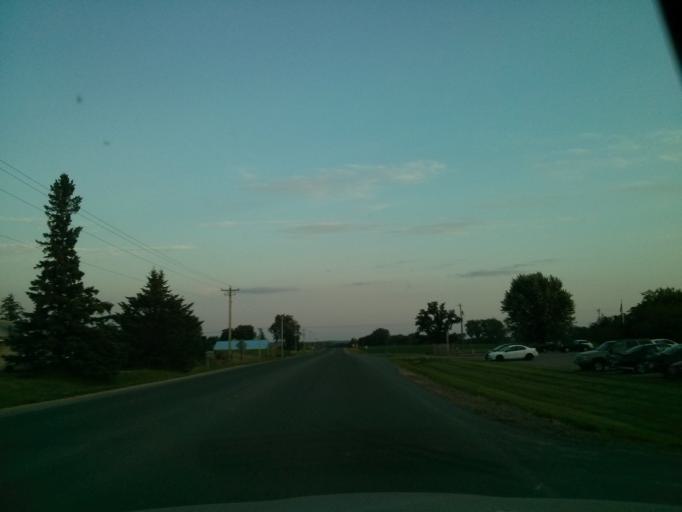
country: US
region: Wisconsin
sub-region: Saint Croix County
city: North Hudson
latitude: 45.0046
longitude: -92.6755
